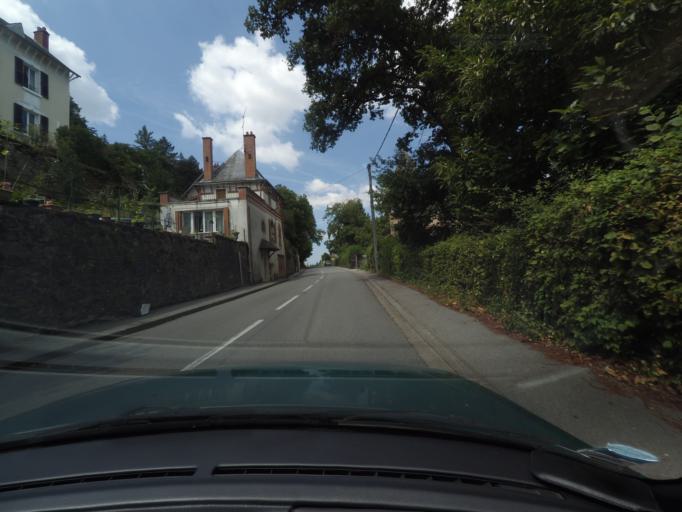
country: FR
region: Limousin
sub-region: Departement de la Haute-Vienne
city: Isle
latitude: 45.7764
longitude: 1.2082
